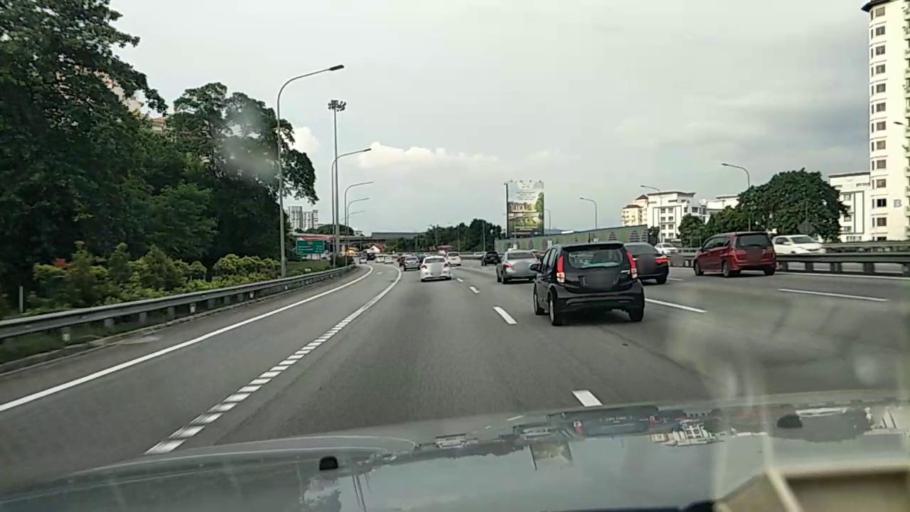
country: MY
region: Selangor
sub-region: Petaling
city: Petaling Jaya
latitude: 3.1074
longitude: 101.5908
